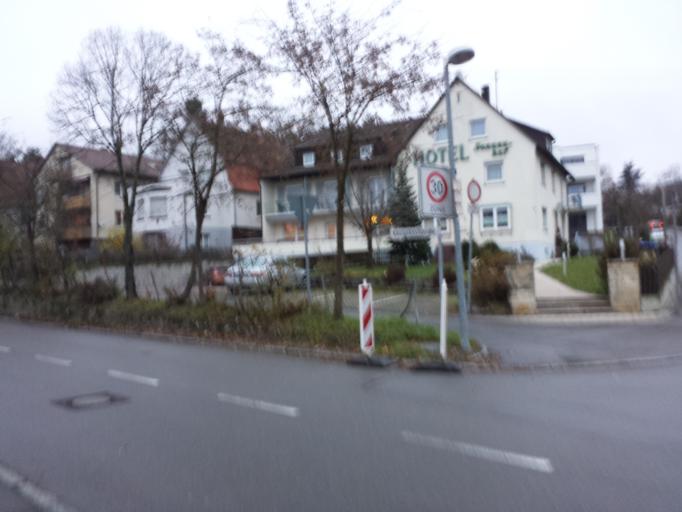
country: DE
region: Baden-Wuerttemberg
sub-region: Regierungsbezirk Stuttgart
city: Sindelfingen
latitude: 48.7081
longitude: 9.0180
